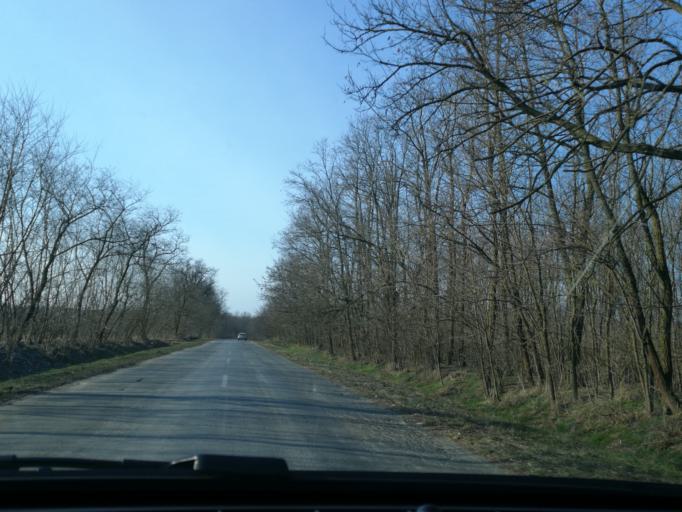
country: HU
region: Szabolcs-Szatmar-Bereg
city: Levelek
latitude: 48.0326
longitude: 21.9718
